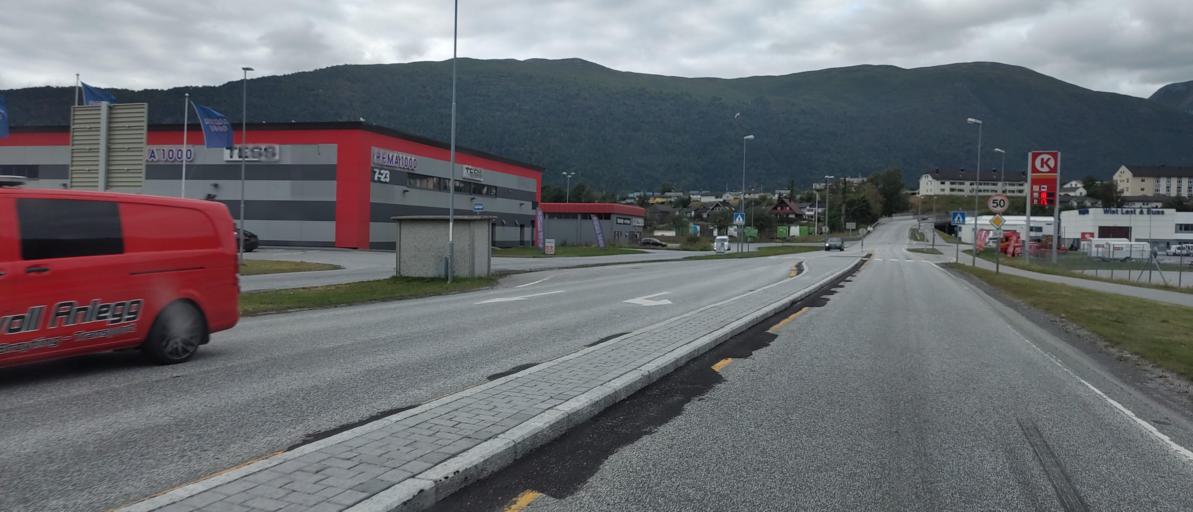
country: NO
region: More og Romsdal
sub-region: Rauma
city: Andalsnes
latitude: 62.5588
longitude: 7.6831
